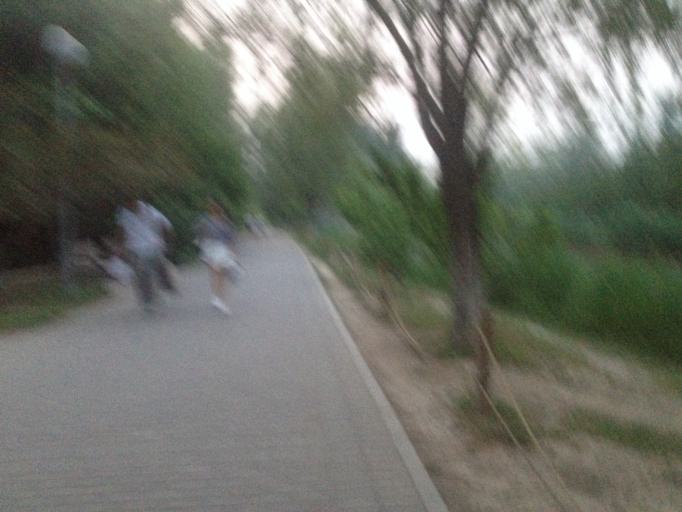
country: CN
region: Beijing
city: Datun
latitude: 40.0102
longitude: 116.3913
